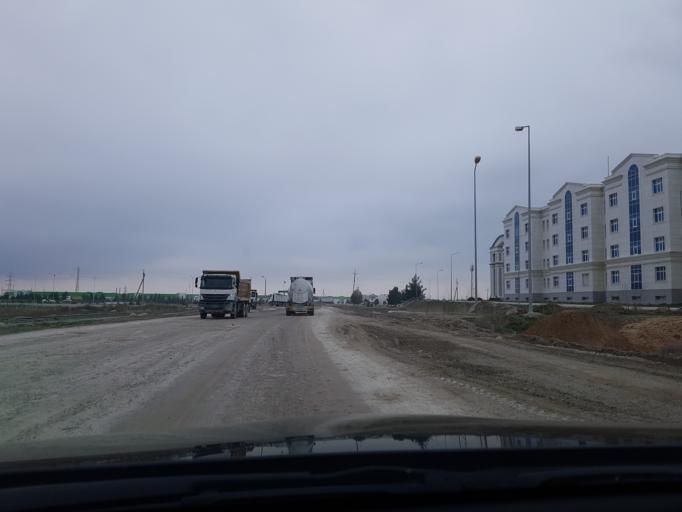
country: TM
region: Ahal
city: Abadan
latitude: 38.1650
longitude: 57.9297
